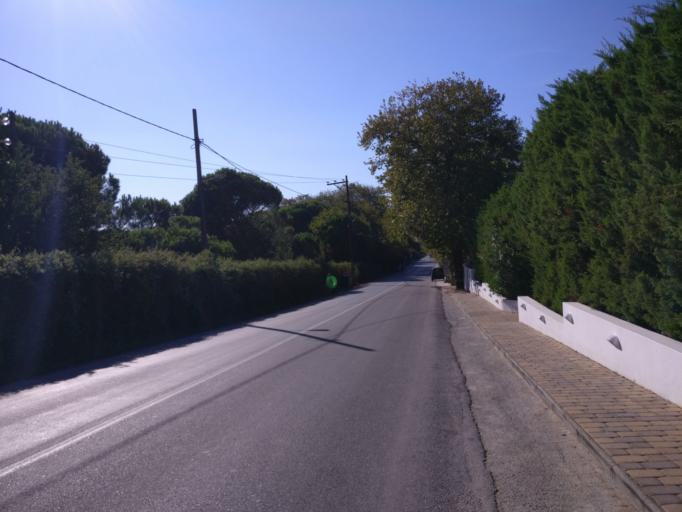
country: GR
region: Thessaly
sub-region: Nomos Magnisias
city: Skiathos
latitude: 39.1521
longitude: 23.4068
